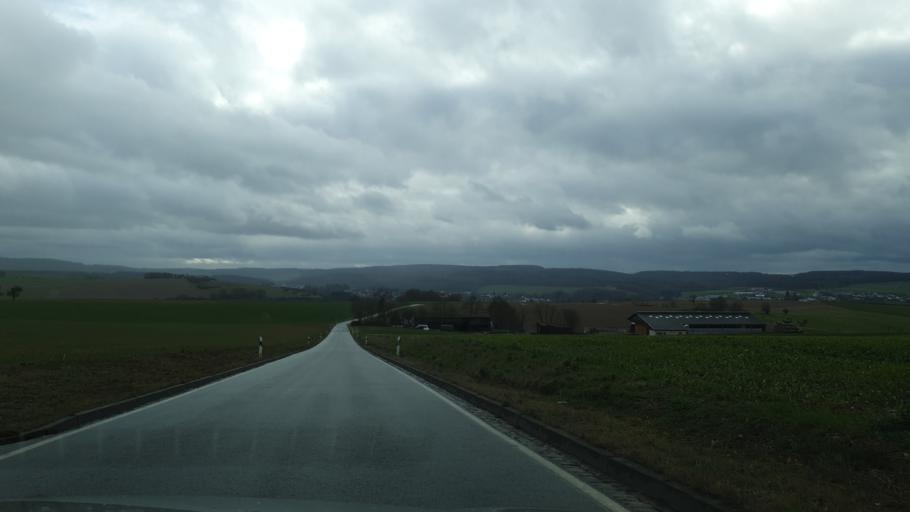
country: DE
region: Rheinland-Pfalz
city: Buch
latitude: 50.2151
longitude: 7.8709
